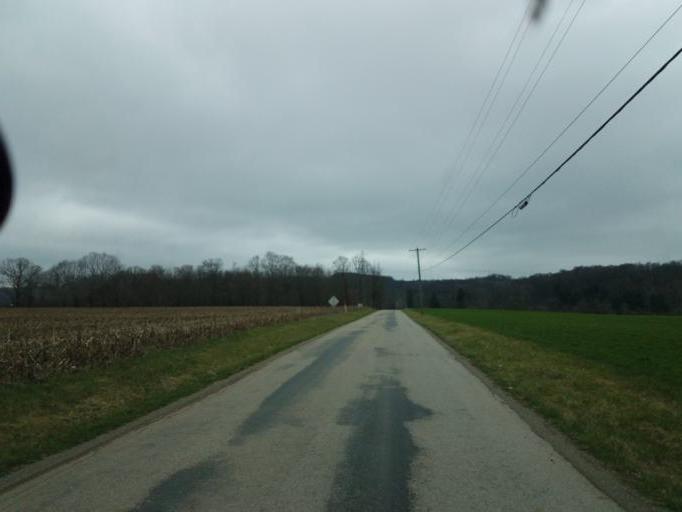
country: US
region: Ohio
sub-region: Sandusky County
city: Bellville
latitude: 40.6078
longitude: -82.4713
